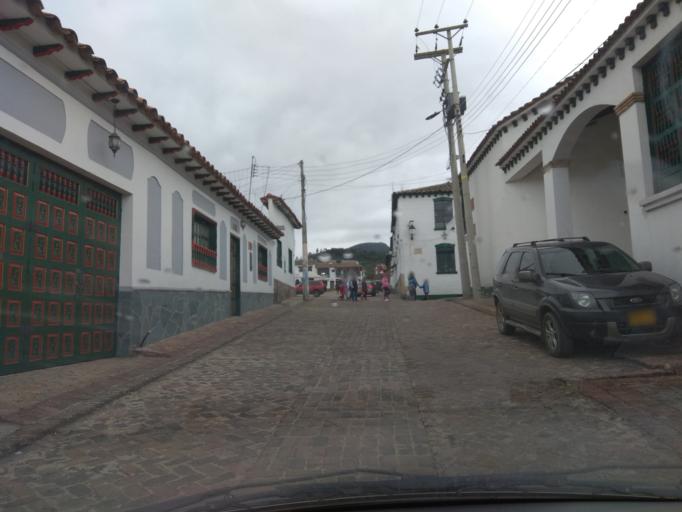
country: CO
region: Boyaca
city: Mongui
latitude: 5.7230
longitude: -72.8497
